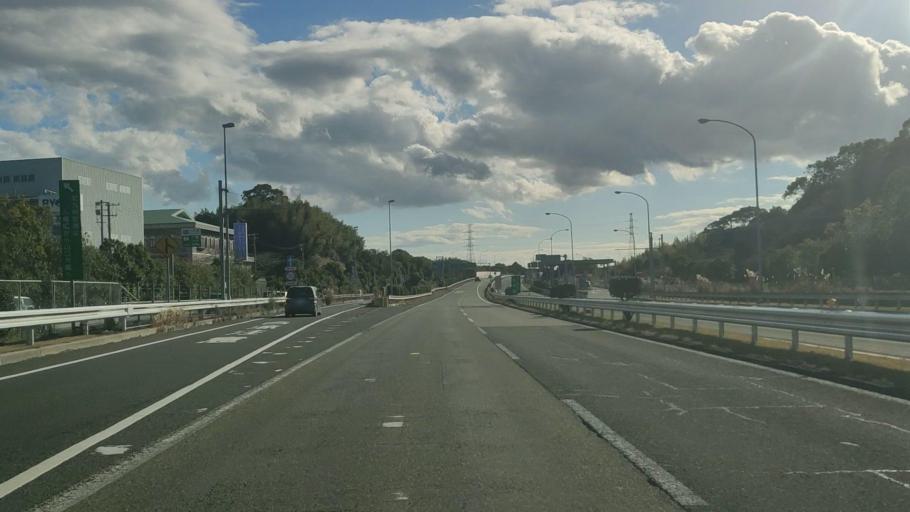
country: JP
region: Fukuoka
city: Nogata
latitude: 33.7878
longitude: 130.7460
